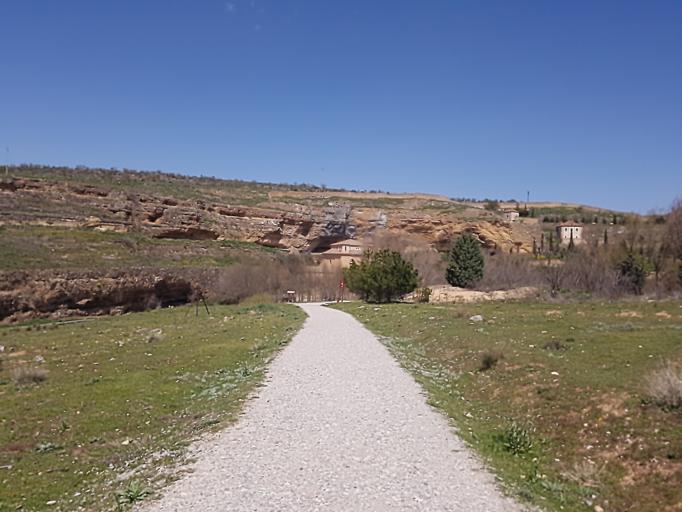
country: ES
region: Castille and Leon
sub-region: Provincia de Segovia
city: Segovia
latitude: 40.9544
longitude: -4.1359
